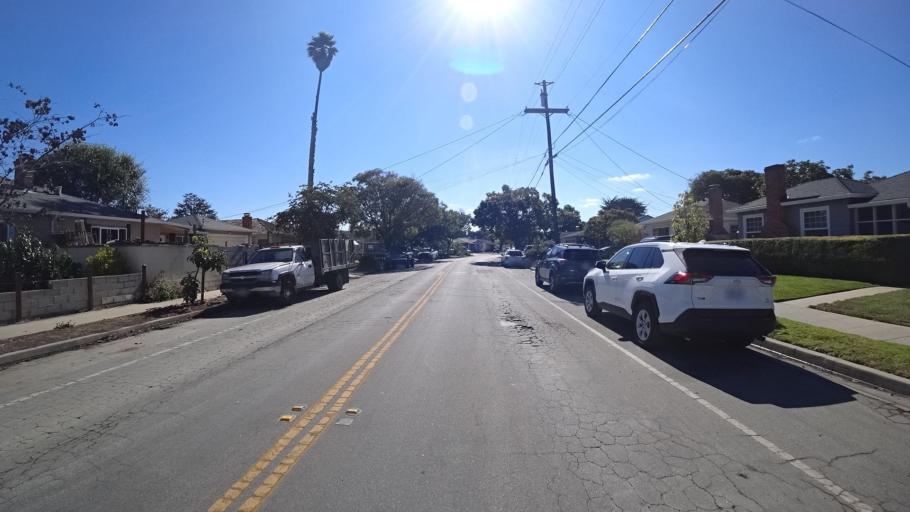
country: US
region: California
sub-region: Monterey County
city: Salinas
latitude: 36.6794
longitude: -121.6722
